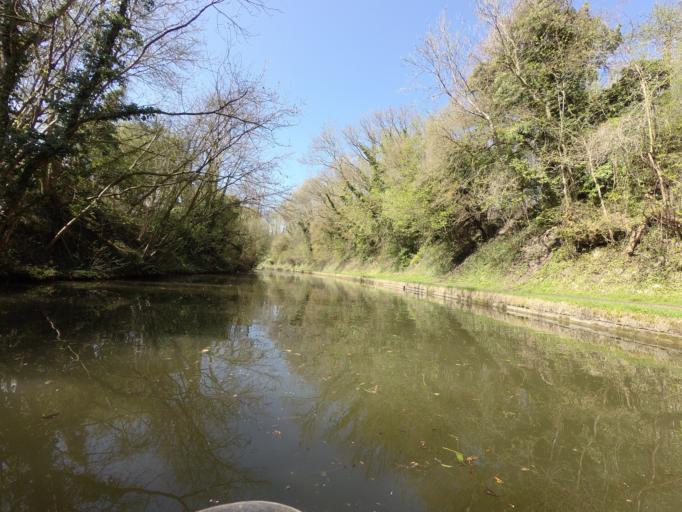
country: GB
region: England
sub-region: Hertfordshire
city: Tring
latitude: 51.7972
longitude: -0.6203
